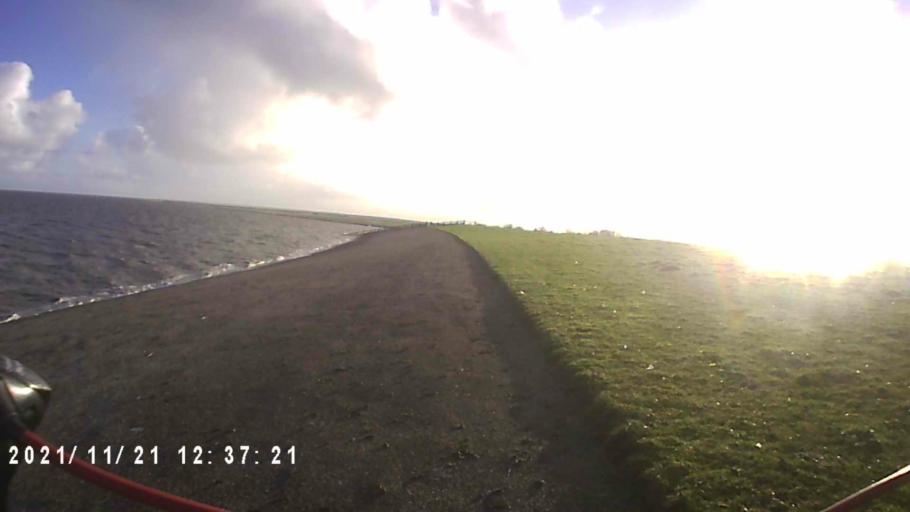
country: NL
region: Friesland
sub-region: Gemeente Dongeradeel
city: Anjum
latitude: 53.4065
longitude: 6.0721
